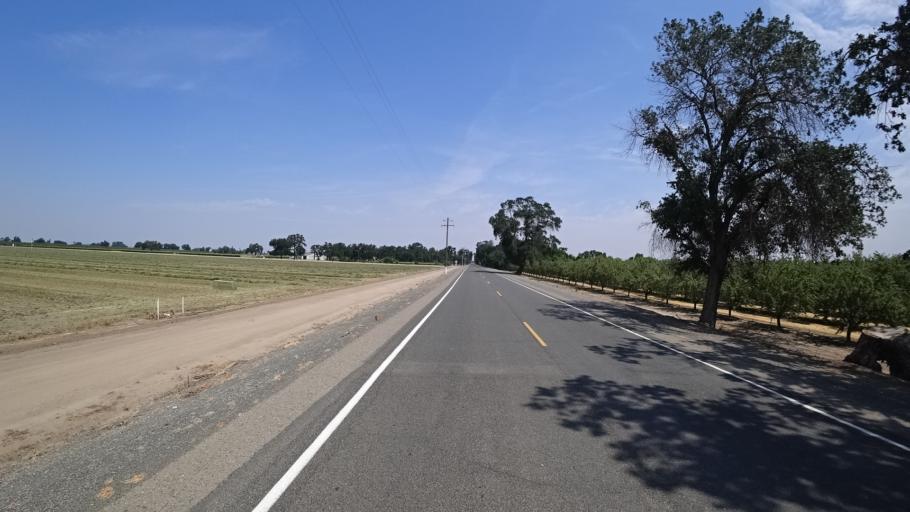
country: US
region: California
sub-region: Kings County
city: Lemoore
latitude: 36.3621
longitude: -119.7810
